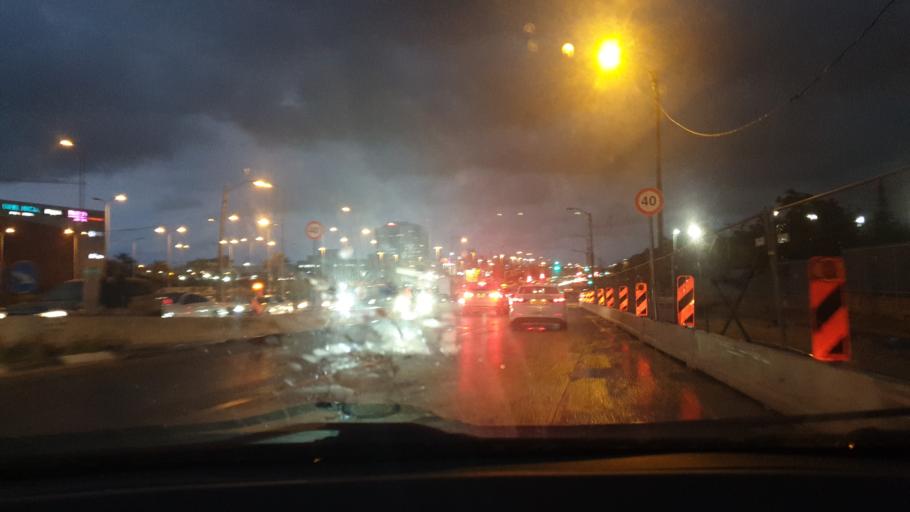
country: IL
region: Central District
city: Rishon LeZiyyon
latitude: 31.9824
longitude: 34.7720
